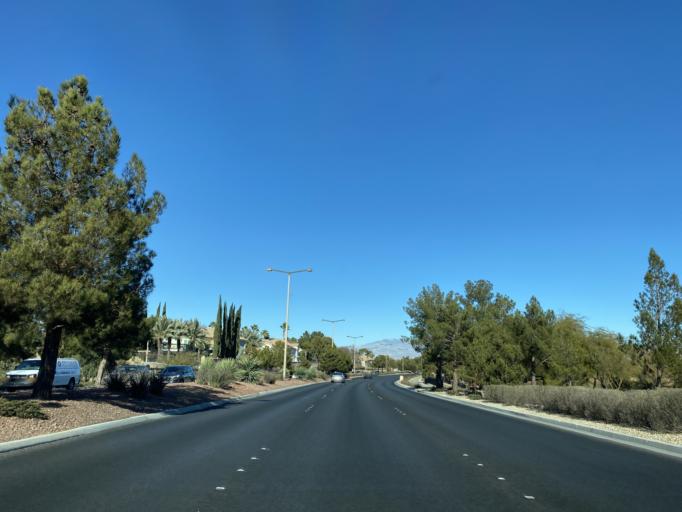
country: US
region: Nevada
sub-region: Clark County
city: Summerlin South
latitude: 36.1899
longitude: -115.2876
